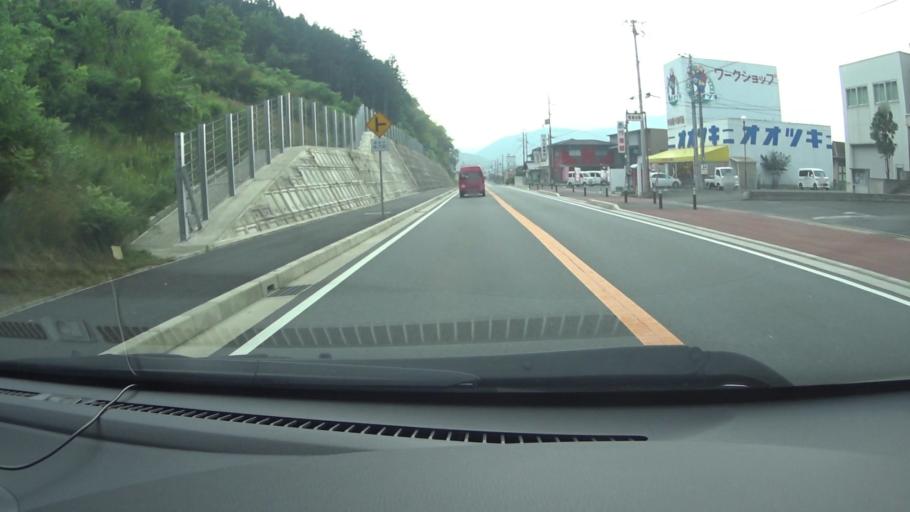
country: JP
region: Kyoto
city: Ayabe
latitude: 35.3042
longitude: 135.2732
